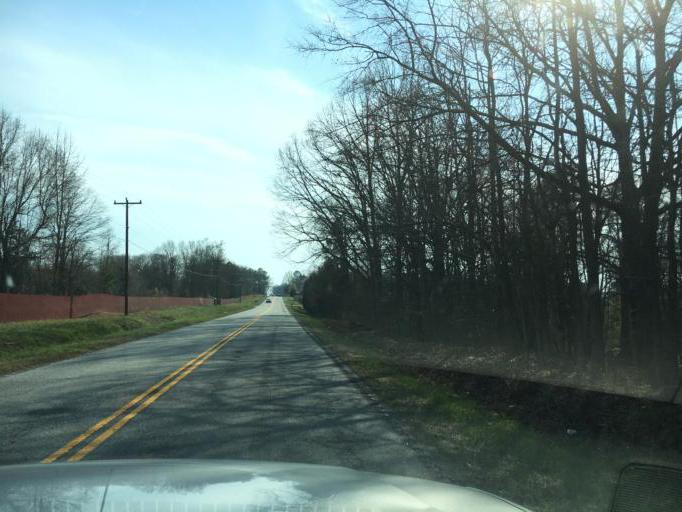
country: US
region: South Carolina
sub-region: Spartanburg County
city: Mayo
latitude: 35.1643
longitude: -81.8448
